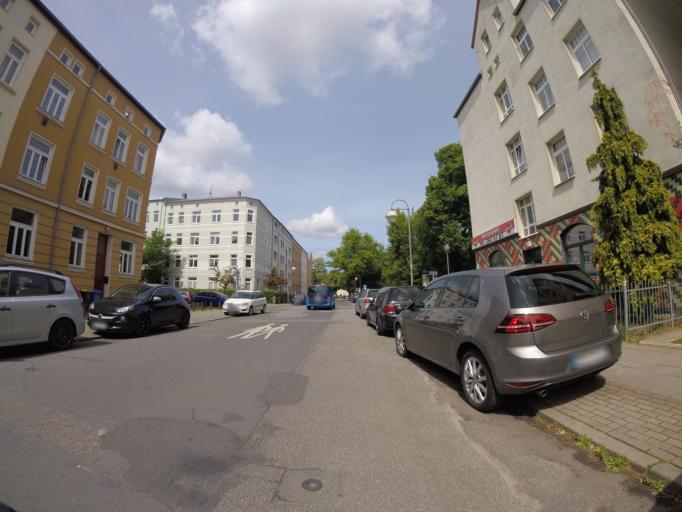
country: DE
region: Mecklenburg-Vorpommern
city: Rostock
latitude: 54.0895
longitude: 12.1085
